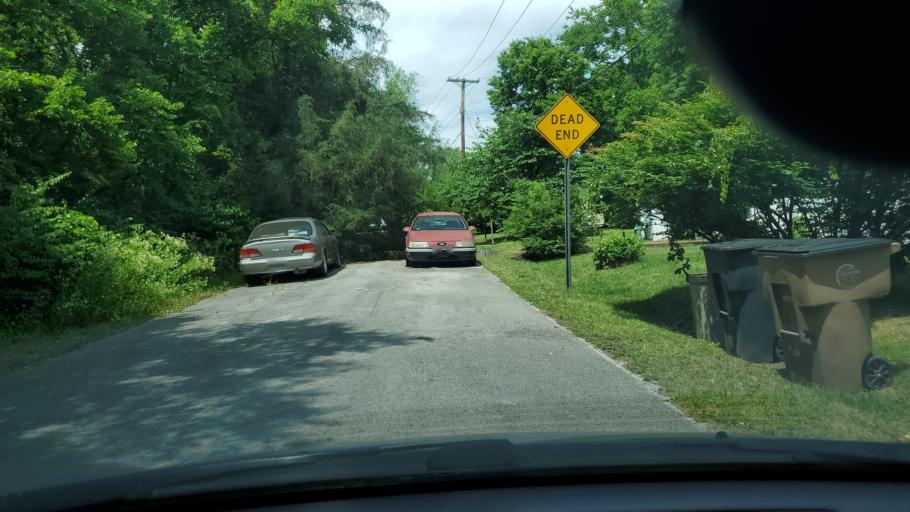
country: US
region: Tennessee
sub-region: Davidson County
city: Nashville
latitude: 36.2287
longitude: -86.7314
